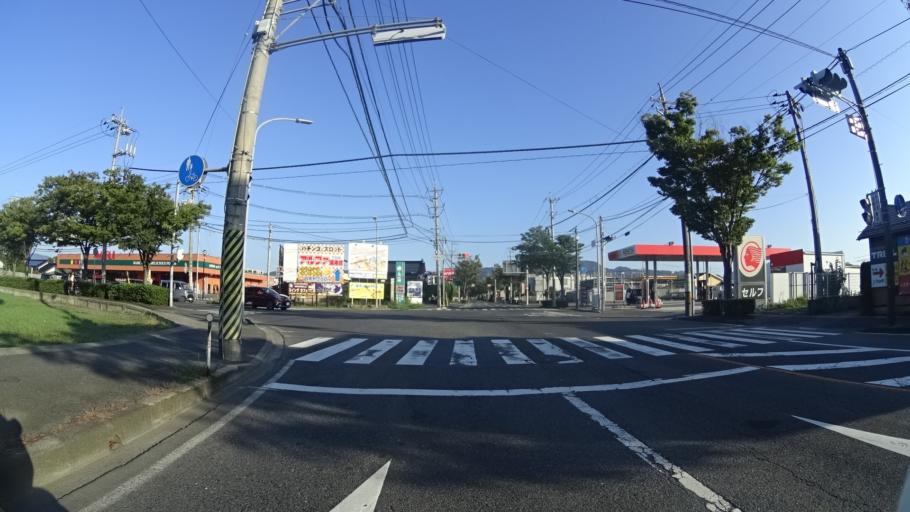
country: JP
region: Shimane
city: Sakaiminato
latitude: 35.5221
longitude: 133.2135
